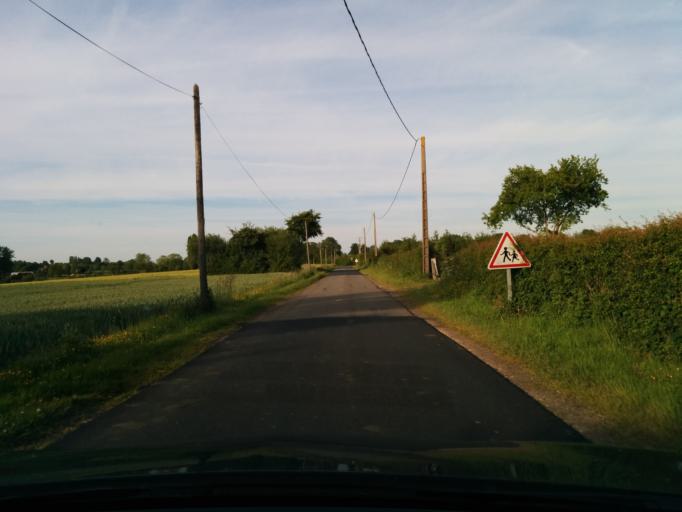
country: FR
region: Haute-Normandie
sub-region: Departement de la Seine-Maritime
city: Neufchatel-en-Bray
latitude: 49.6679
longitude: 1.4722
